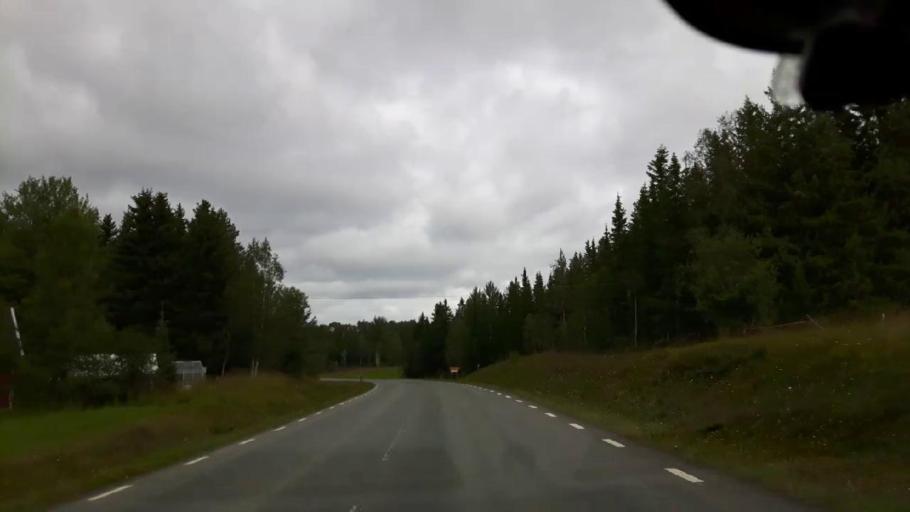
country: SE
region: Jaemtland
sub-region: Krokoms Kommun
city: Valla
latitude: 63.5048
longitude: 13.8955
